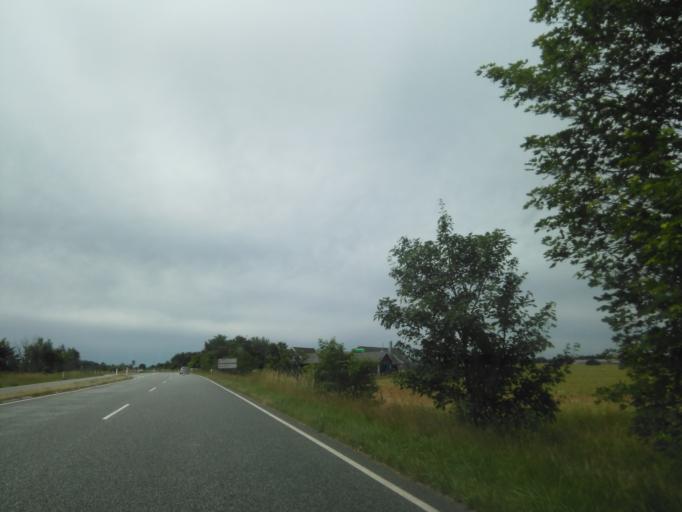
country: DK
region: Central Jutland
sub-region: Arhus Kommune
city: Solbjerg
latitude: 56.0317
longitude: 10.0648
